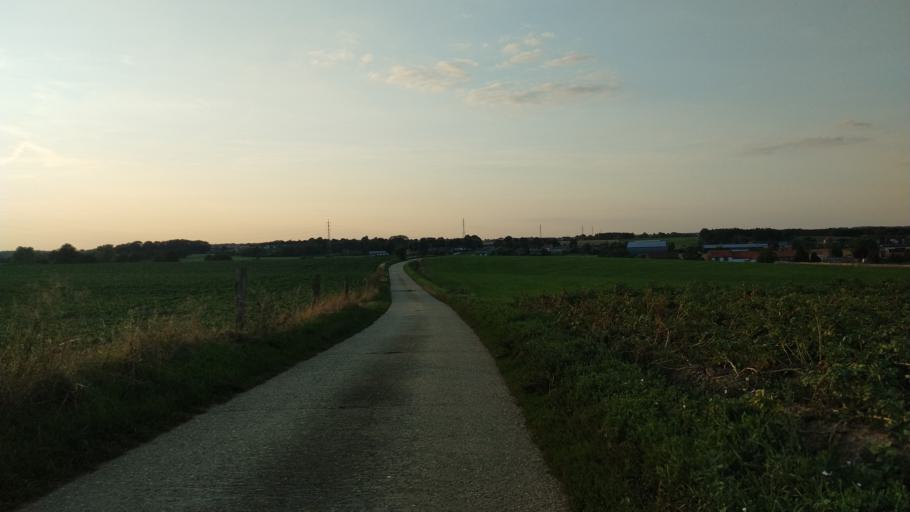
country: BE
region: Flanders
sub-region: Provincie Vlaams-Brabant
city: Lubbeek
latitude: 50.8853
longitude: 4.8100
